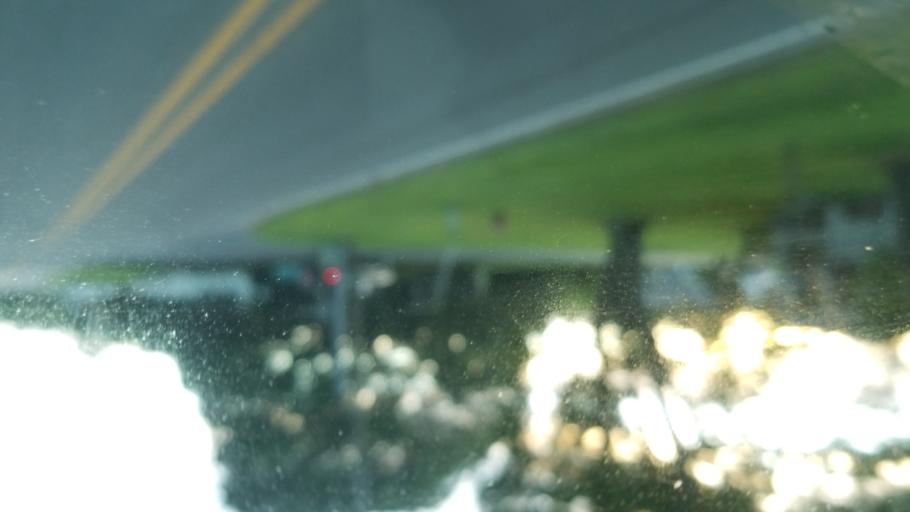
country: US
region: North Carolina
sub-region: Dare County
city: Wanchese
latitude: 35.8430
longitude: -75.6318
